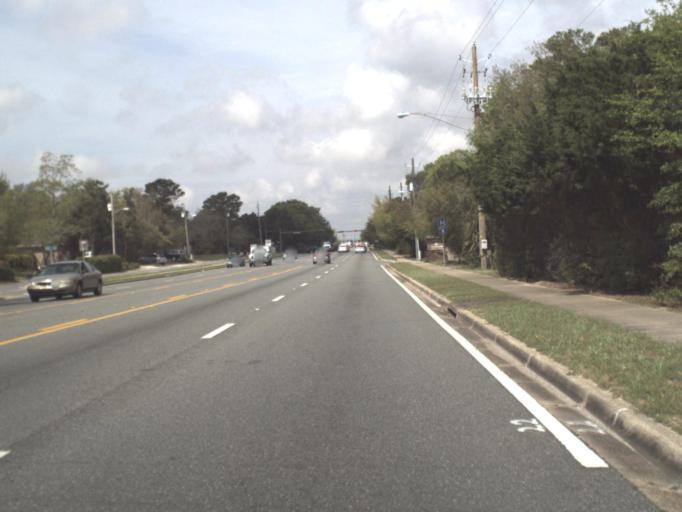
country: US
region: Florida
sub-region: Okaloosa County
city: Ocean City
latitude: 30.4273
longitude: -86.6277
